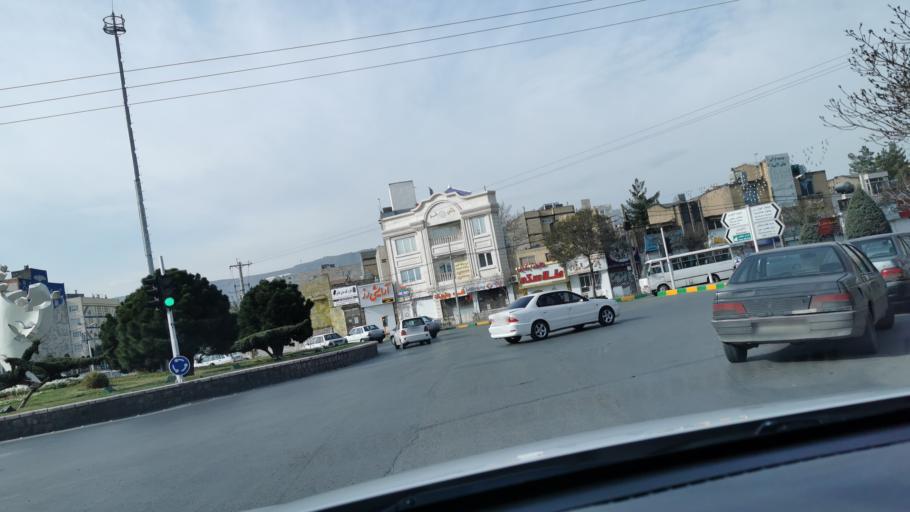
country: IR
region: Razavi Khorasan
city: Mashhad
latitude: 36.3051
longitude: 59.5128
